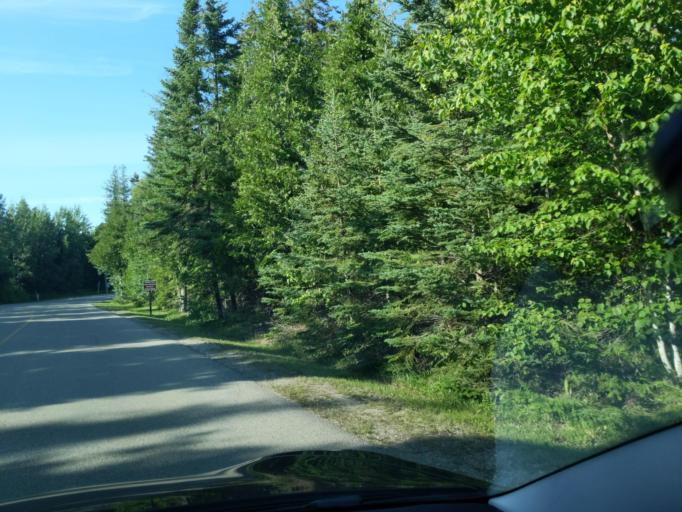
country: US
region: Michigan
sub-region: Mackinac County
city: Saint Ignace
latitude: 45.8544
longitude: -84.7196
